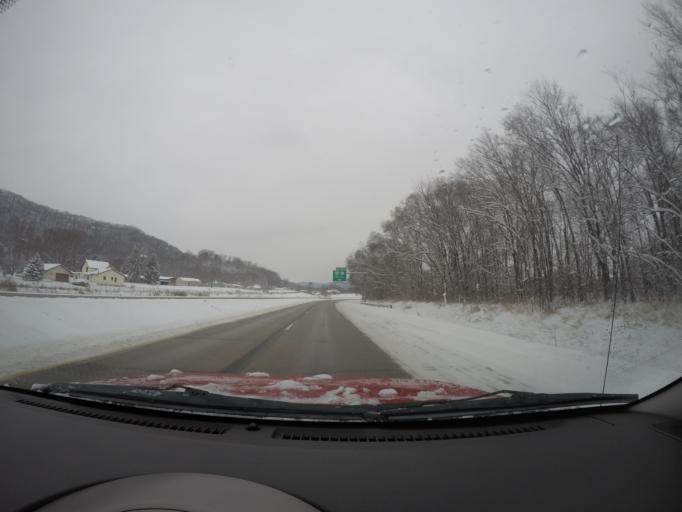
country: US
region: Wisconsin
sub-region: La Crosse County
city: Brice Prairie
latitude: 43.9090
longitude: -91.3569
